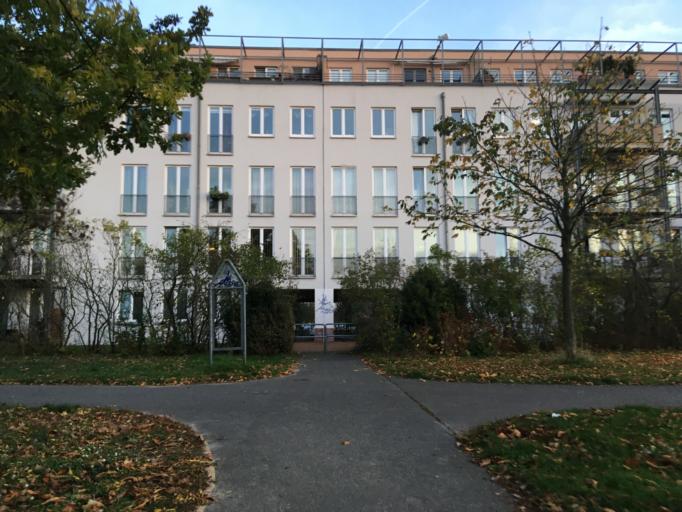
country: DE
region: Berlin
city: Buchholz
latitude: 52.6113
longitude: 13.4187
